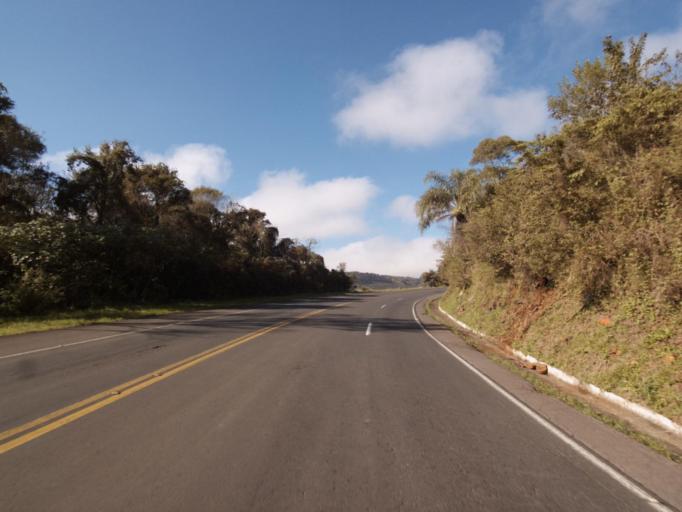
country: BR
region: Rio Grande do Sul
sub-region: Frederico Westphalen
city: Frederico Westphalen
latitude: -27.0853
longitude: -53.2194
